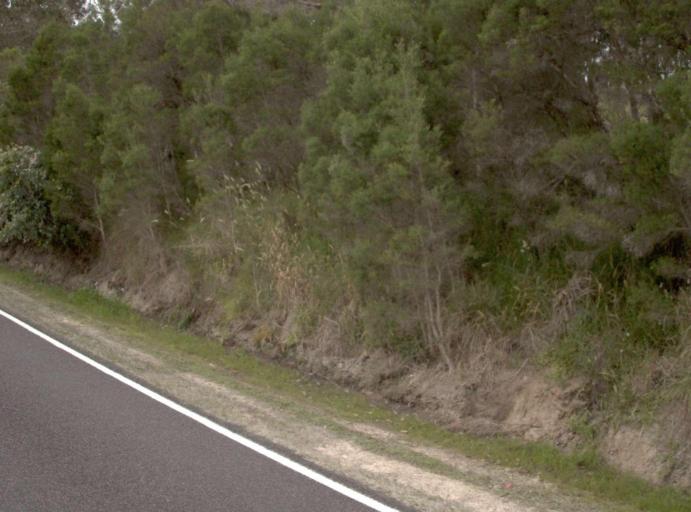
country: AU
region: New South Wales
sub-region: Bombala
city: Bombala
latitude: -37.4798
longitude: 149.1807
